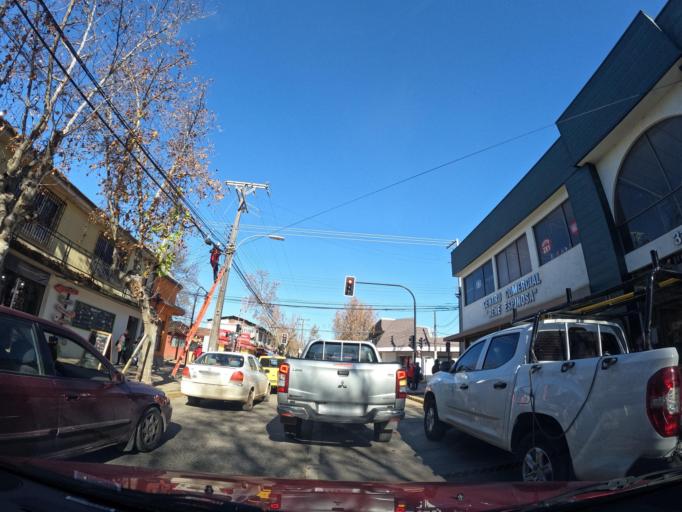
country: CL
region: Maule
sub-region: Provincia de Cauquenes
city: Cauquenes
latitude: -35.9686
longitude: -72.3163
